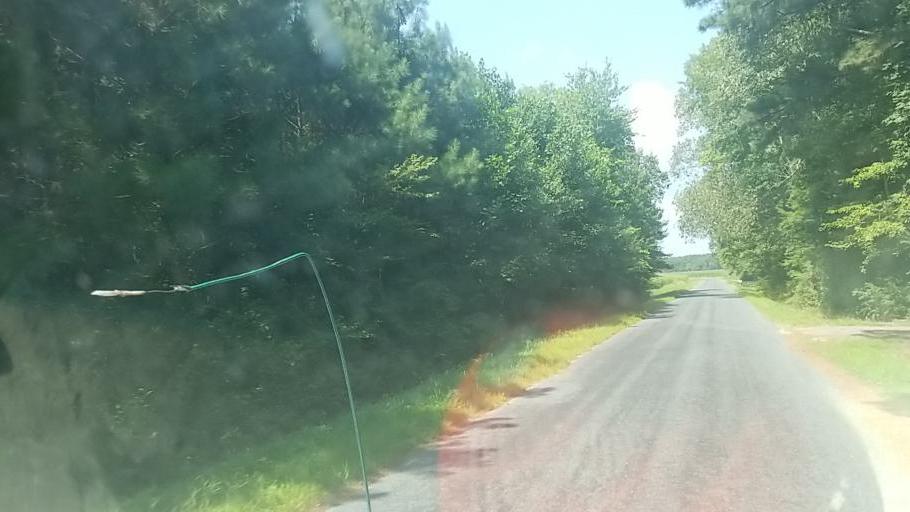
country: US
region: Maryland
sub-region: Worcester County
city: Berlin
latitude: 38.2976
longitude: -75.2878
